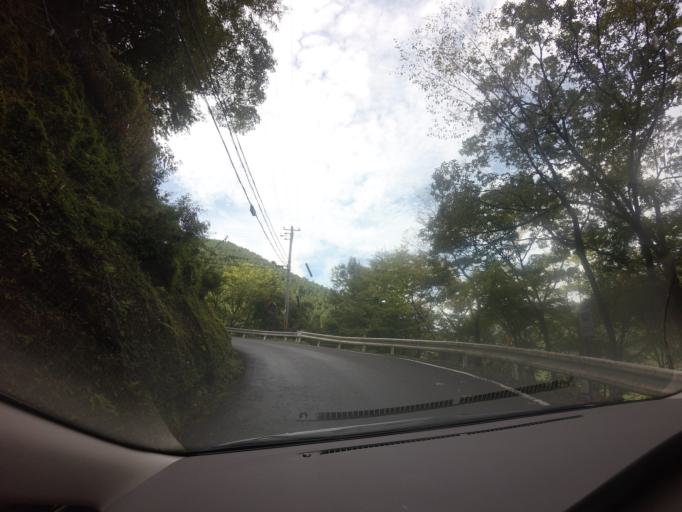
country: JP
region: Wakayama
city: Shingu
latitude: 33.9640
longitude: 135.8477
